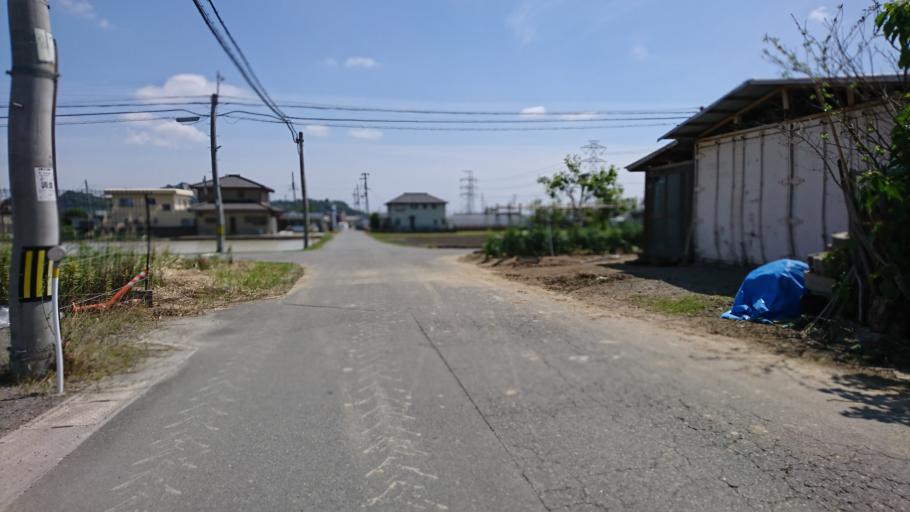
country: JP
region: Hyogo
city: Kakogawacho-honmachi
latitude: 34.7968
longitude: 134.7859
